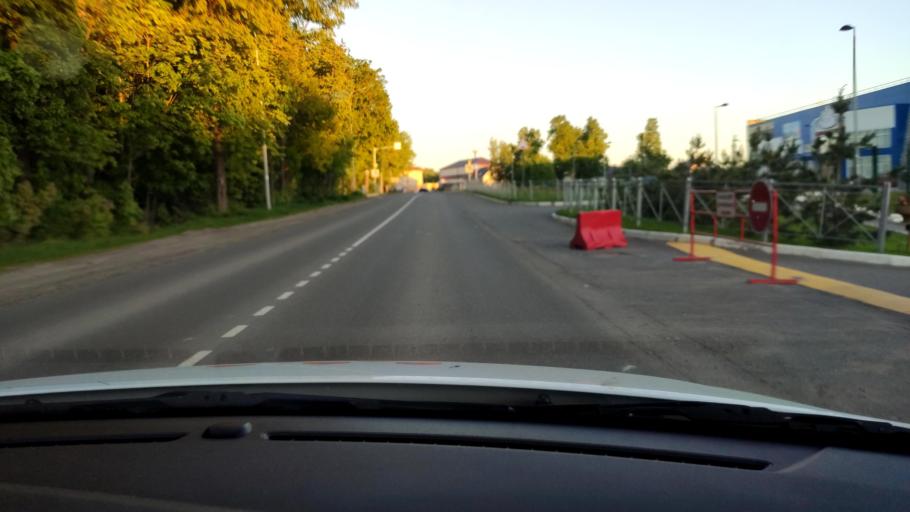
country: RU
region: Tatarstan
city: Vysokaya Gora
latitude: 55.9238
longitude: 49.3048
